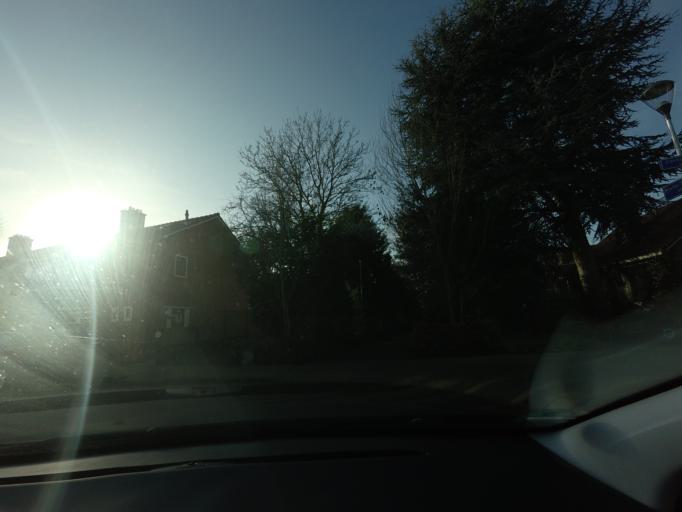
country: NL
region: Utrecht
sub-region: Gemeente Woerden
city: Woerden
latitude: 52.0919
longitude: 4.8738
